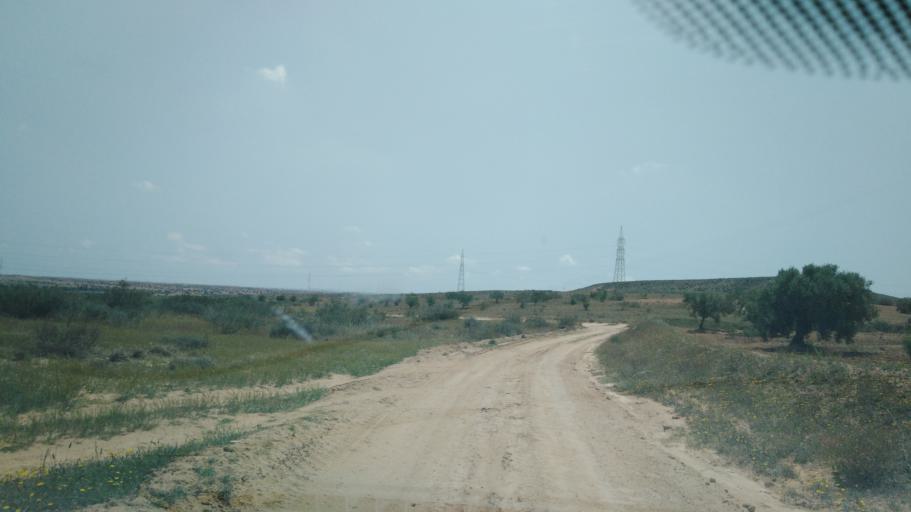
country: TN
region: Safaqis
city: Sfax
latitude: 34.7658
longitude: 10.5815
